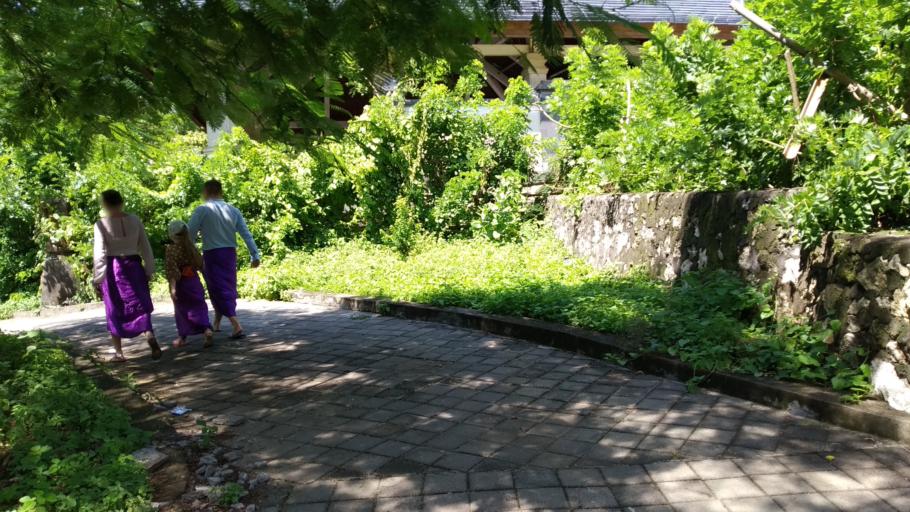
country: ID
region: Bali
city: Pecatu
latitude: -8.8302
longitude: 115.0863
